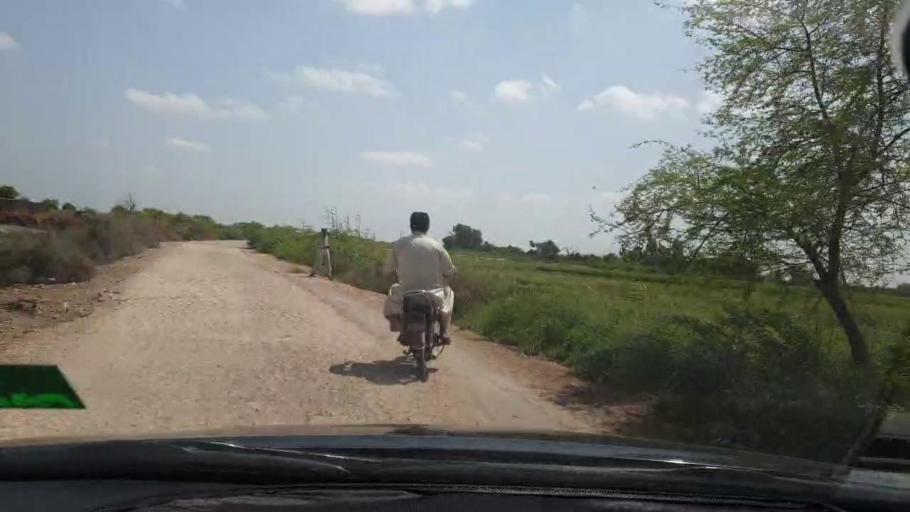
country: PK
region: Sindh
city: Tando Bago
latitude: 24.8787
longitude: 69.0808
